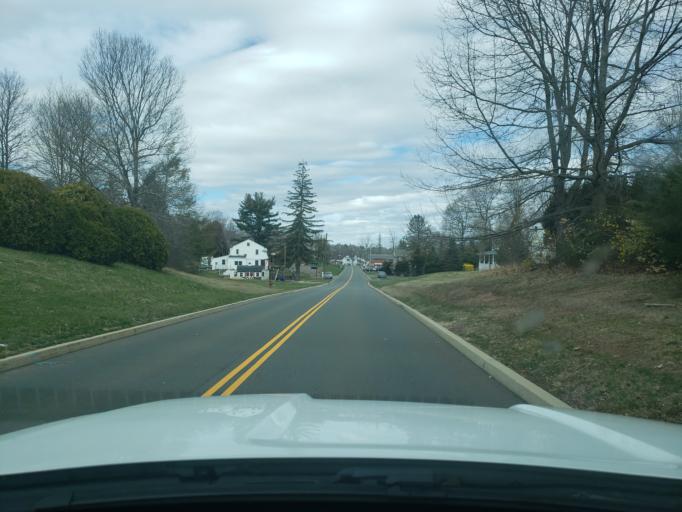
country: US
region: Connecticut
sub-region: Middlesex County
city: Middletown
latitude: 41.5339
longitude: -72.6549
